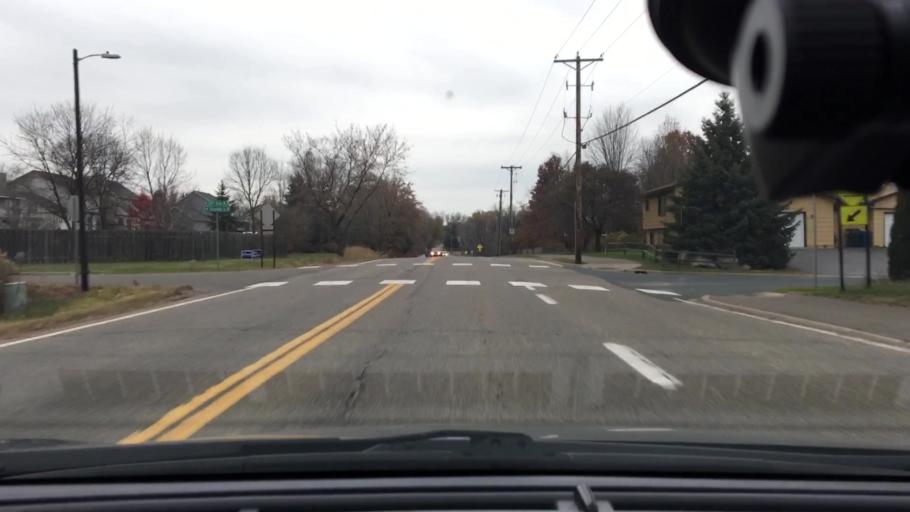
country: US
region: Minnesota
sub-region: Hennepin County
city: Corcoran
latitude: 45.1064
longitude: -93.5118
